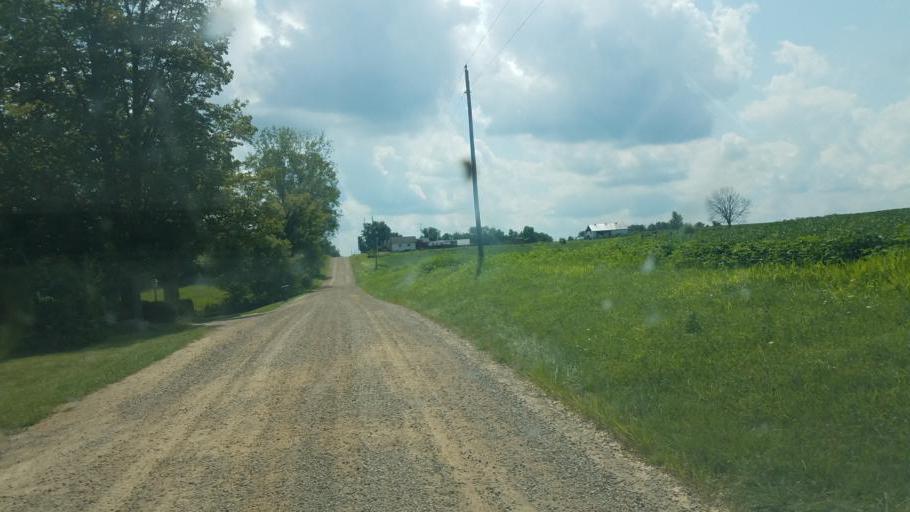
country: US
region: Ohio
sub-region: Knox County
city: Fredericktown
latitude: 40.4145
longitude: -82.5829
